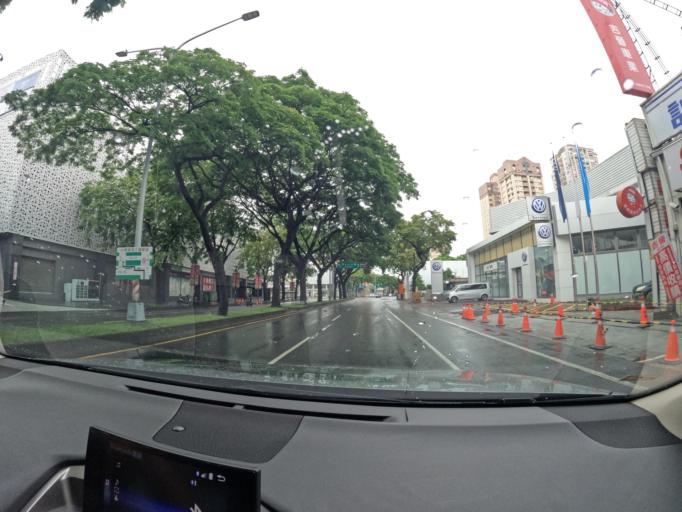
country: TW
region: Kaohsiung
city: Kaohsiung
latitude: 22.6557
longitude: 120.3142
